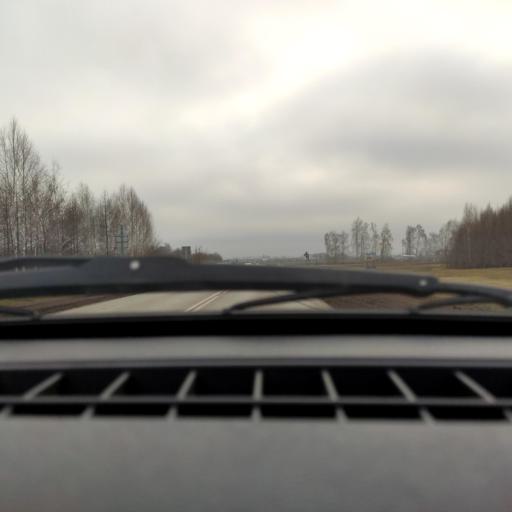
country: RU
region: Bashkortostan
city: Chishmy
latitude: 54.5768
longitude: 55.3612
